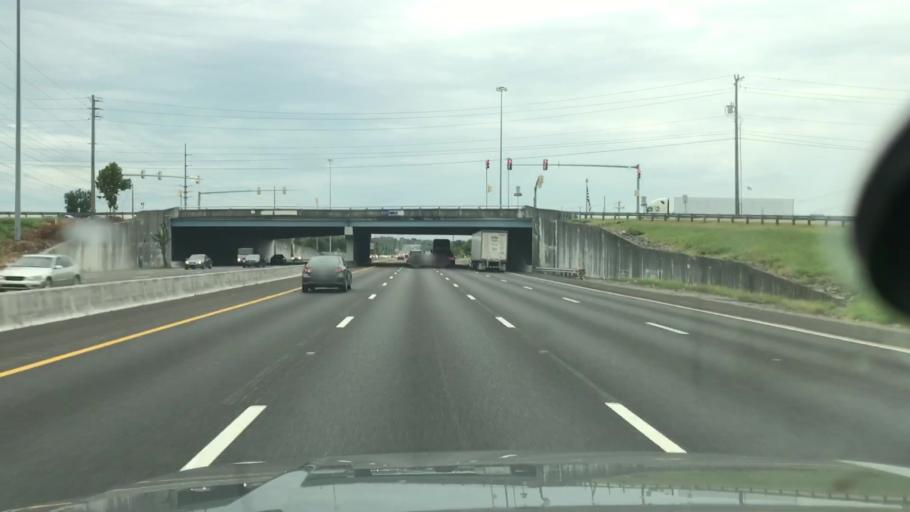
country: US
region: Tennessee
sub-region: Davidson County
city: Lakewood
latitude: 36.2179
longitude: -86.6929
